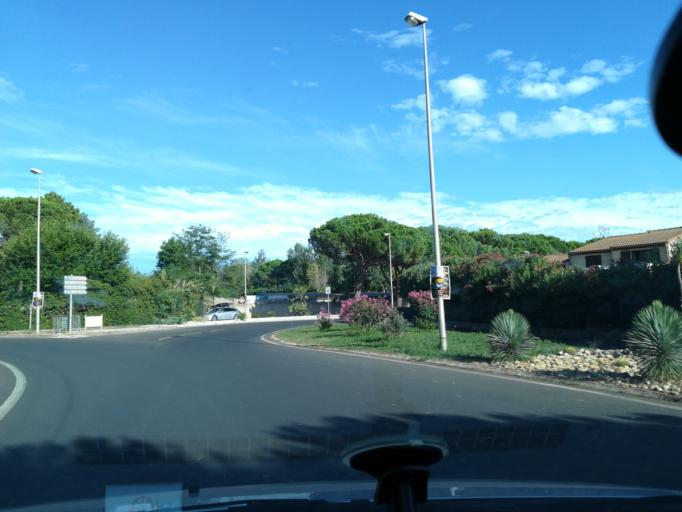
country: FR
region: Languedoc-Roussillon
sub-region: Departement de l'Herault
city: Portiragnes
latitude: 43.2831
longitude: 3.3623
